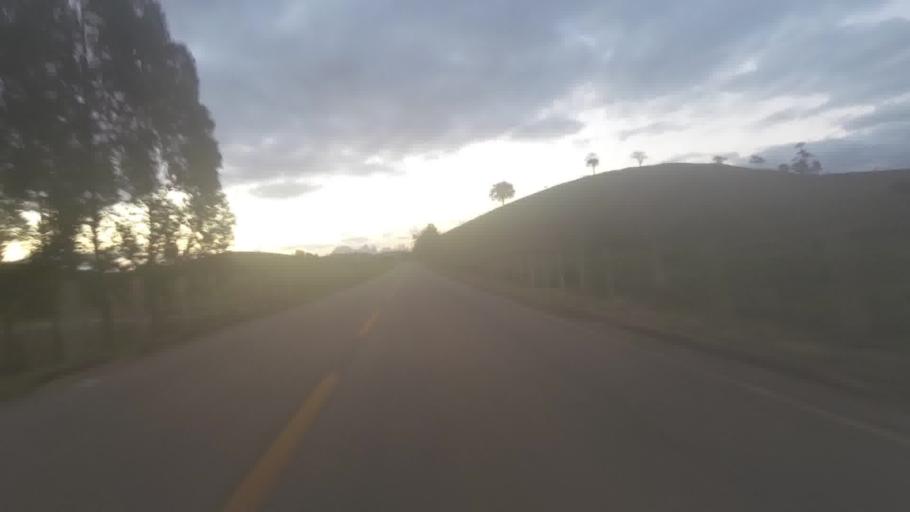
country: BR
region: Espirito Santo
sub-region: Itapemirim
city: Itapemirim
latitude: -20.9662
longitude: -40.8718
